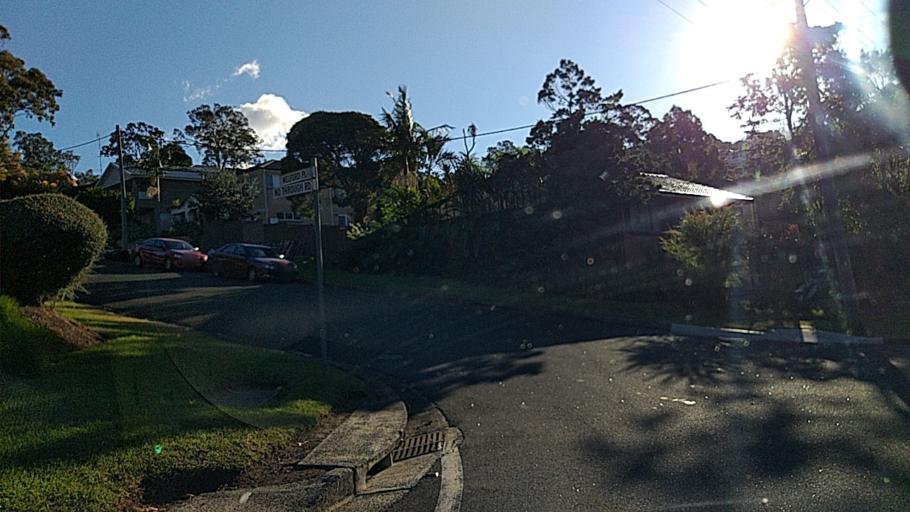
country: AU
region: New South Wales
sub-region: Wollongong
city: Mount Keira
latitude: -34.4277
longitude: 150.8475
